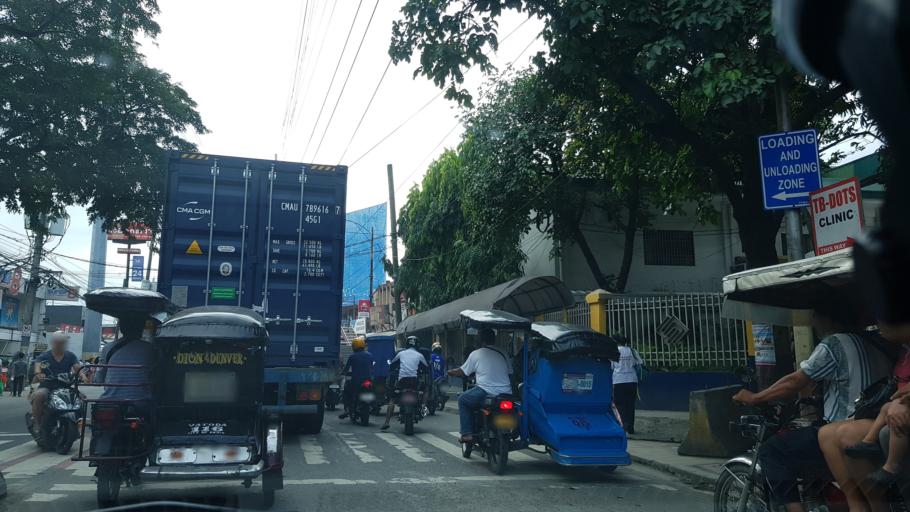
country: PH
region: Calabarzon
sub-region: Province of Rizal
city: Pateros
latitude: 14.5512
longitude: 121.0756
